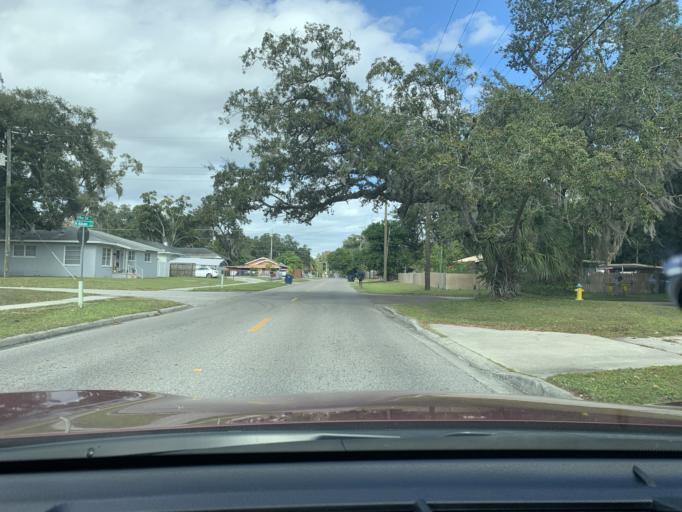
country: US
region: Florida
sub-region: Hillsborough County
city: Tampa
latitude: 27.9679
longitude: -82.4931
